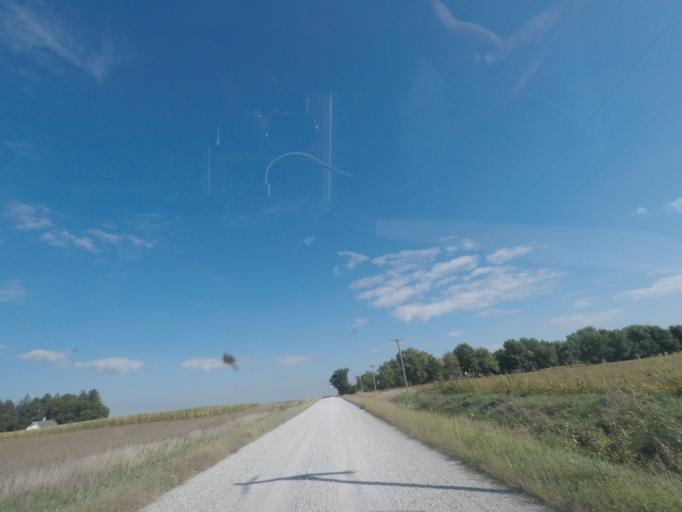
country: US
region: Iowa
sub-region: Story County
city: Nevada
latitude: 42.0348
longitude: -93.4252
